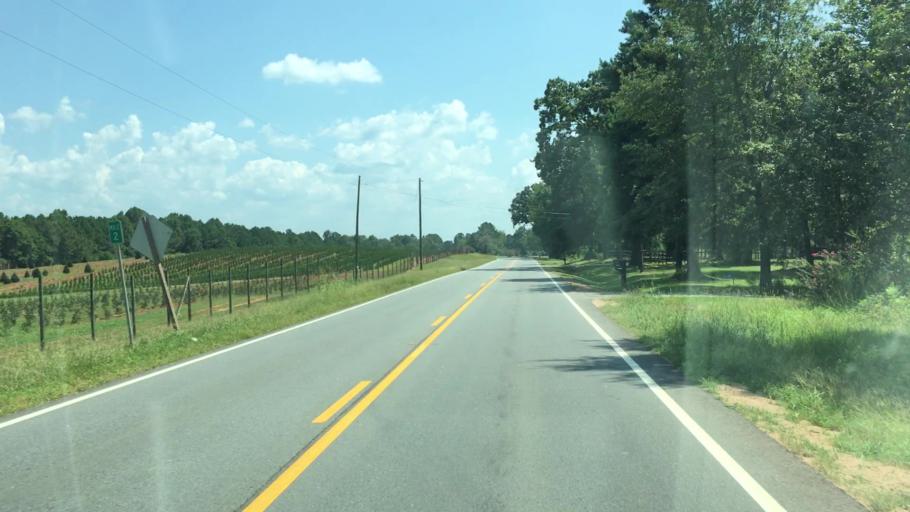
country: US
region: Georgia
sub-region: Oconee County
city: Watkinsville
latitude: 33.7474
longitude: -83.4333
